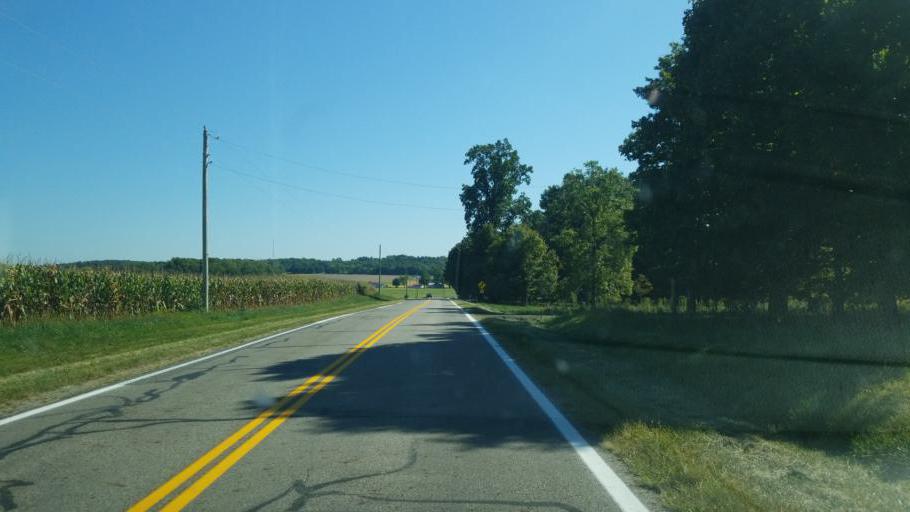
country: US
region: Ohio
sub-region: Champaign County
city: North Lewisburg
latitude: 40.2191
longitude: -83.6385
